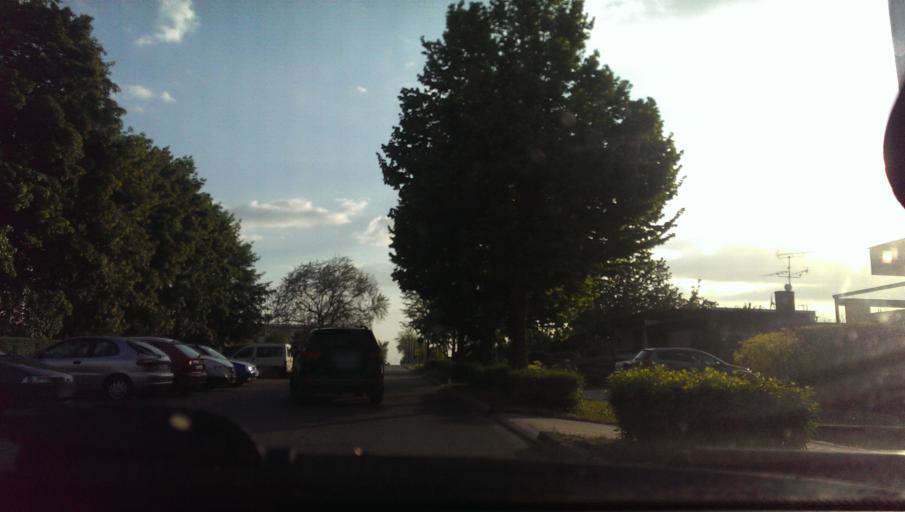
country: CZ
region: Zlin
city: Kunovice
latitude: 49.0605
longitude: 17.4797
